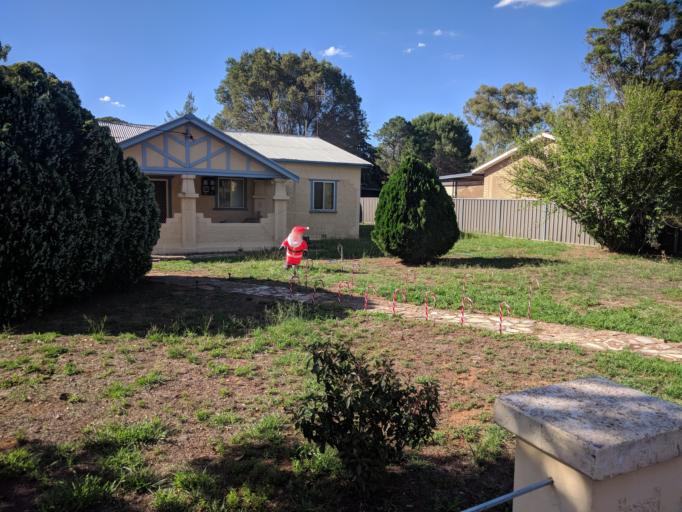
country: AU
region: New South Wales
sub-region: Mid-Western Regional
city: Gulgong
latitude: -32.3658
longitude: 149.5247
